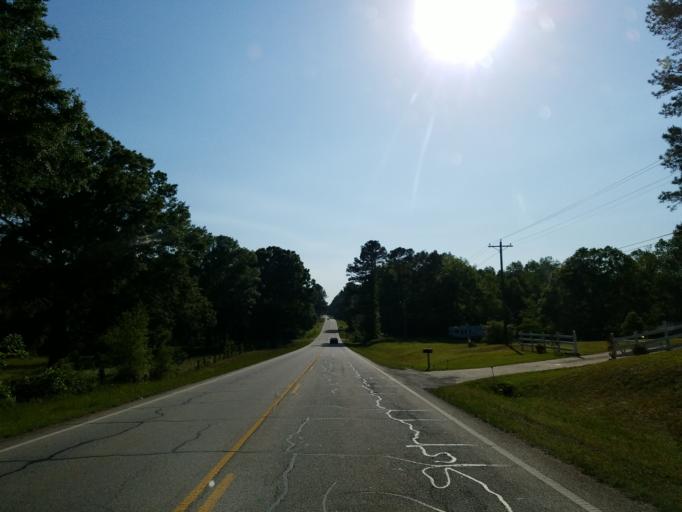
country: US
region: Georgia
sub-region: Carroll County
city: Villa Rica
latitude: 33.8501
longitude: -84.9535
